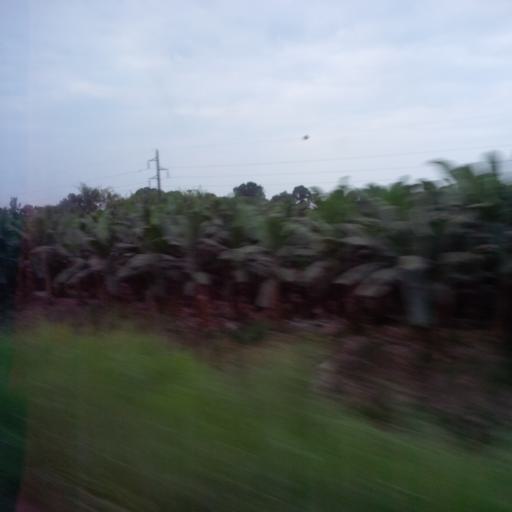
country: EC
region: Canar
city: La Troncal
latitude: -2.3438
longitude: -79.3722
